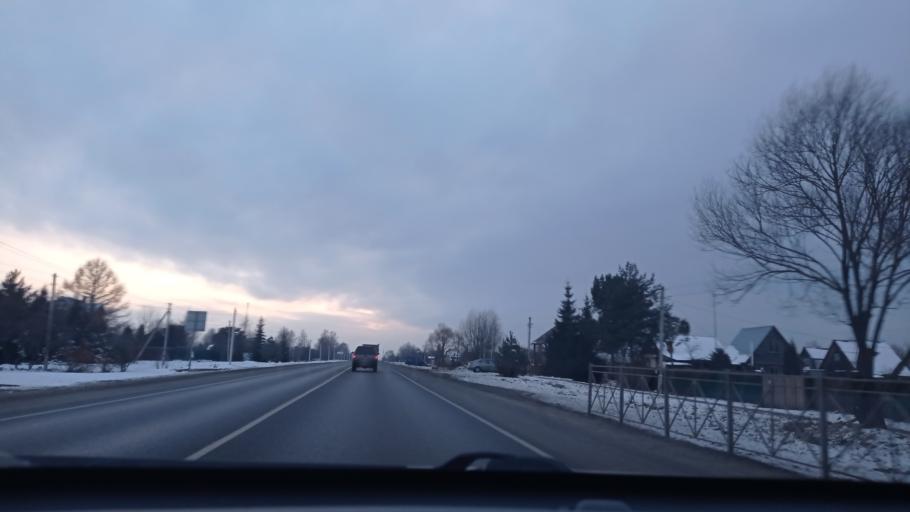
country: RU
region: Moskovskaya
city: Ateptsevo
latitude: 55.1963
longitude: 36.9172
